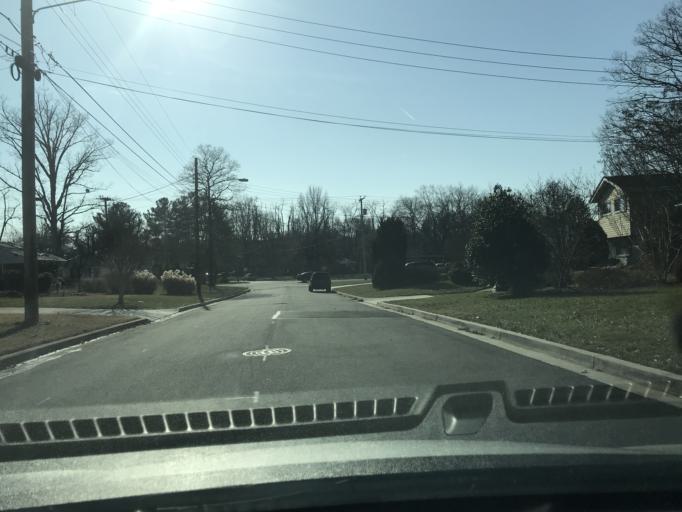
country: US
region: Virginia
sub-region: City of Fairfax
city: Fairfax
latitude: 38.8568
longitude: -77.3261
